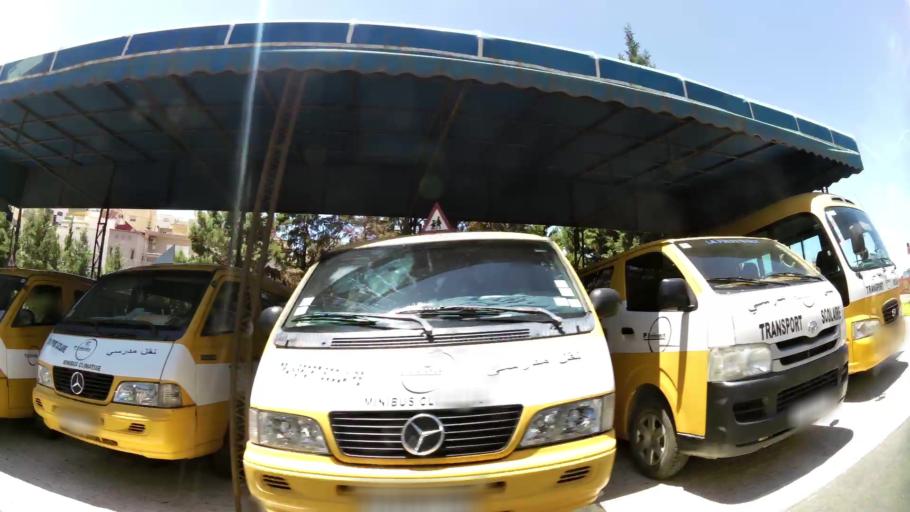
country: MA
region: Meknes-Tafilalet
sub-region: Meknes
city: Meknes
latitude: 33.9076
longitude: -5.5504
